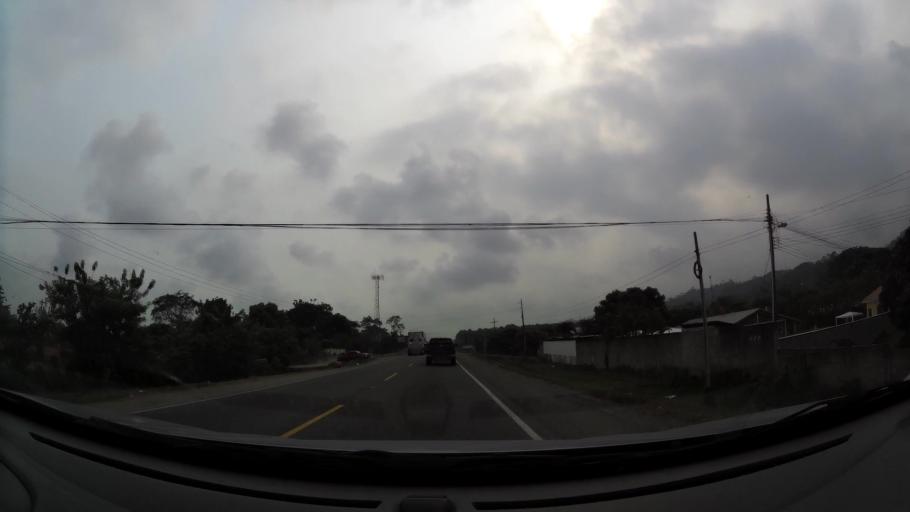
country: HN
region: Yoro
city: Guaimitas
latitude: 15.4841
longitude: -87.7653
